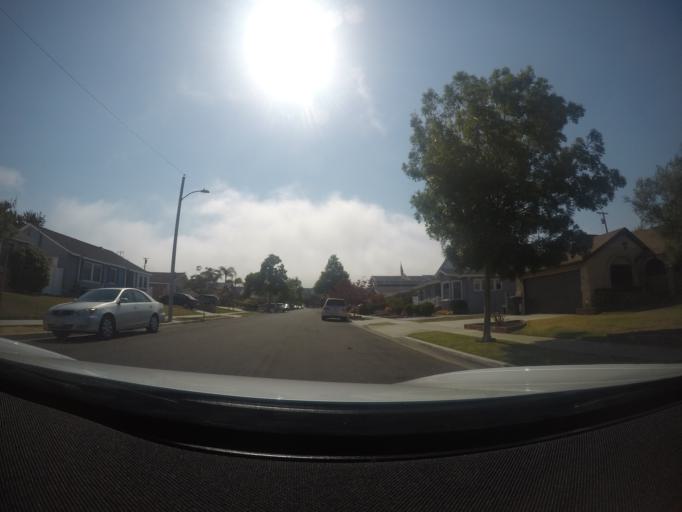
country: US
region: California
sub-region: Los Angeles County
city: Torrance
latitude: 33.8277
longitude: -118.3666
